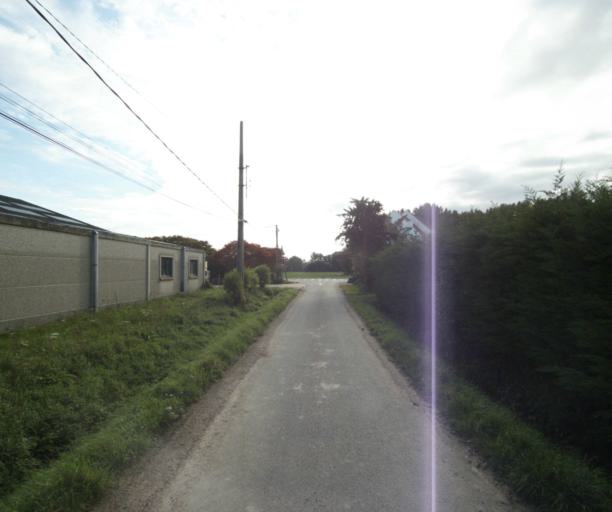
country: FR
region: Nord-Pas-de-Calais
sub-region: Departement du Nord
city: Ennetieres-en-Weppes
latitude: 50.6383
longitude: 2.9230
